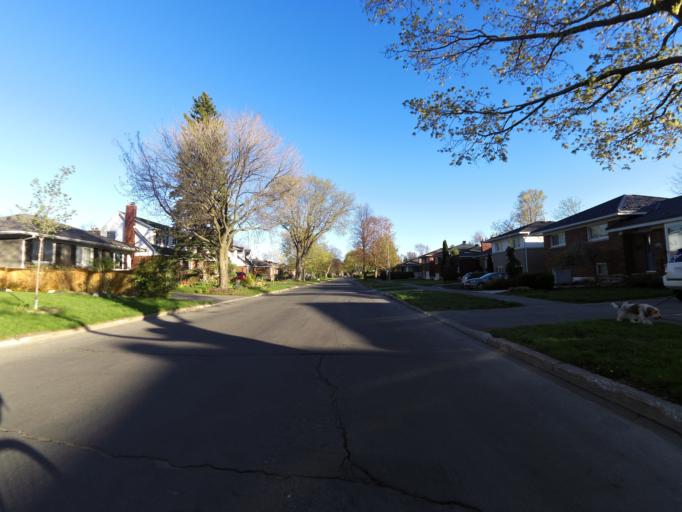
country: CA
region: Ontario
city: Bells Corners
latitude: 45.3607
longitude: -75.7629
